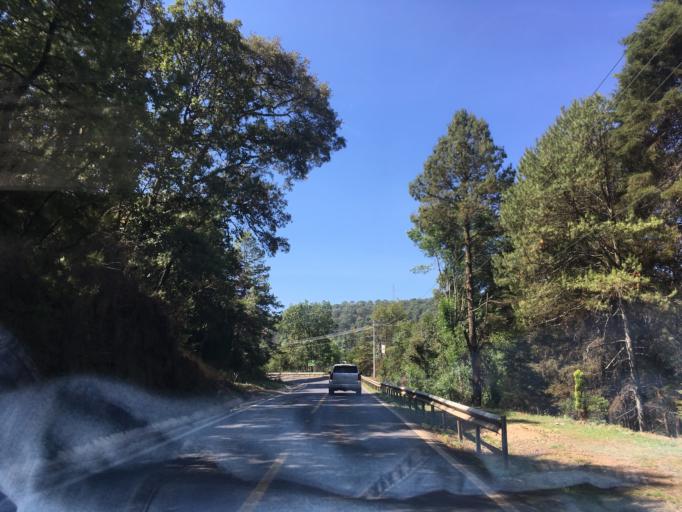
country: MX
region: Michoacan
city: Charo
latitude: 19.6621
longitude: -101.0027
